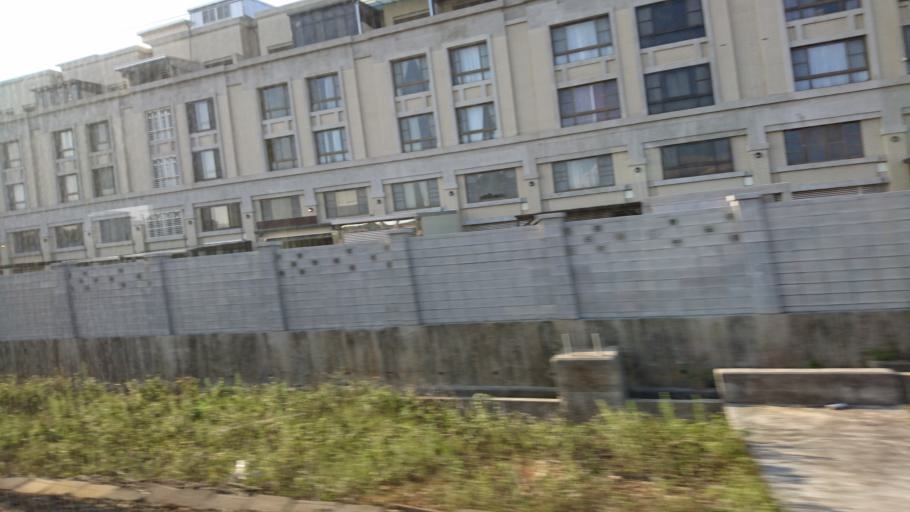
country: TW
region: Taiwan
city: Taoyuan City
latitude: 24.9651
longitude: 121.2467
